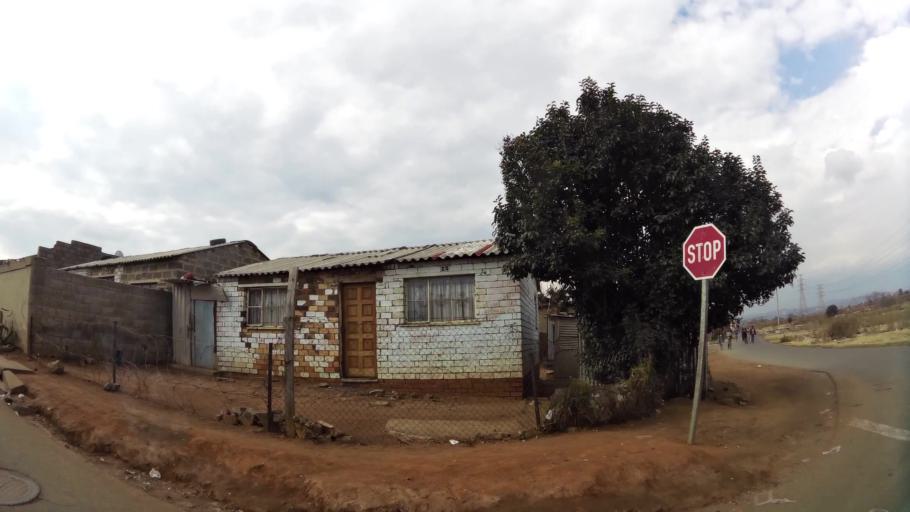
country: ZA
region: Gauteng
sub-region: City of Johannesburg Metropolitan Municipality
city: Soweto
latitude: -26.2369
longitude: 27.8674
